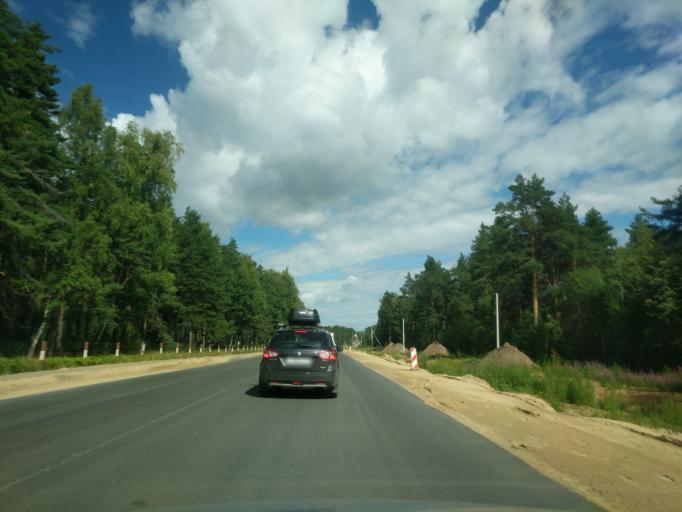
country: RU
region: Jaroslavl
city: Levashevo
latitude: 57.6684
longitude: 40.5776
